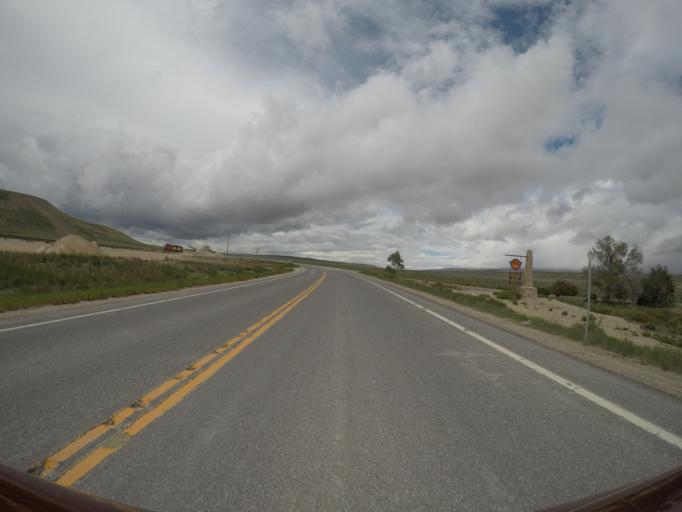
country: US
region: Wyoming
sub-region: Park County
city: Powell
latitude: 45.0593
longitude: -108.6581
